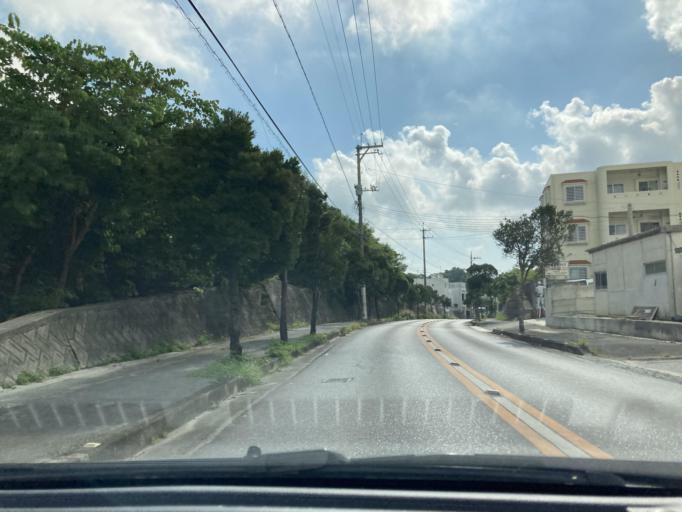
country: JP
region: Okinawa
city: Tomigusuku
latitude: 26.1480
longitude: 127.7608
